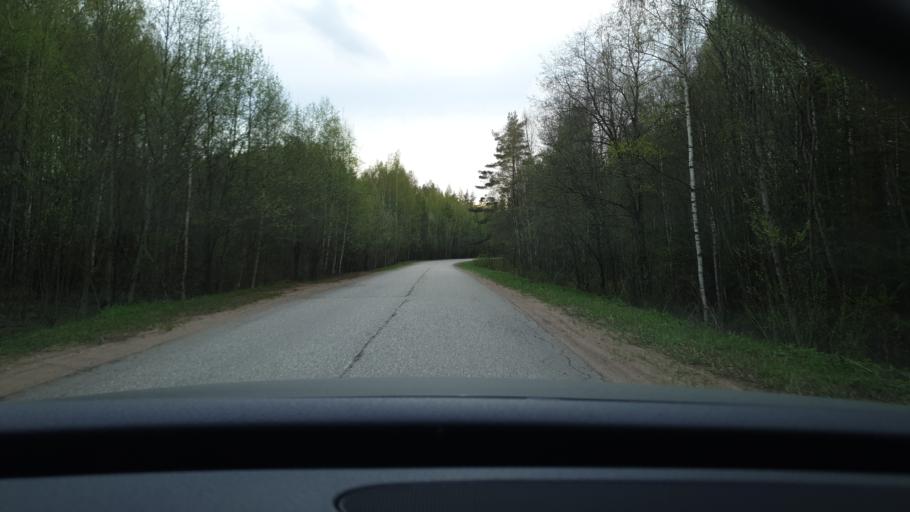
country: RU
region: Tverskaya
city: Bologoye
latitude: 57.9782
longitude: 34.0550
